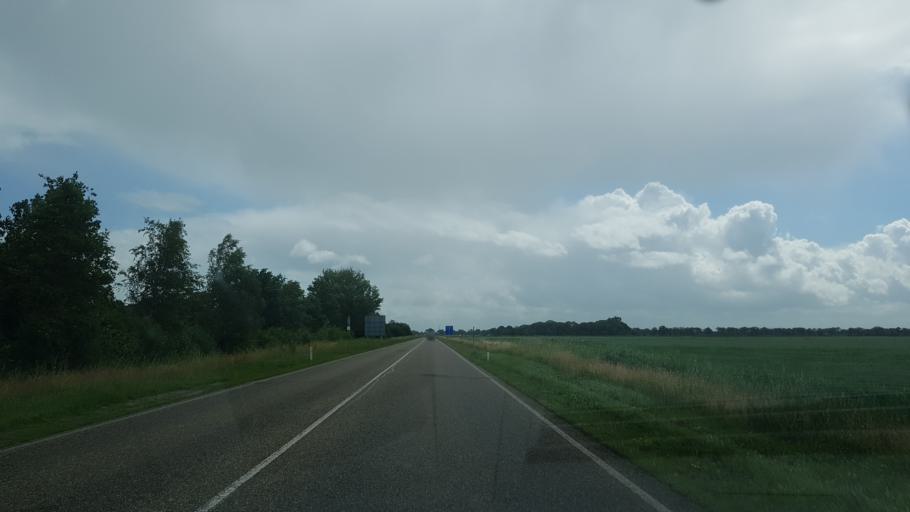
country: NL
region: Friesland
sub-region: Gemeente Dongeradeel
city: Dokkum
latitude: 53.3112
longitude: 5.9982
